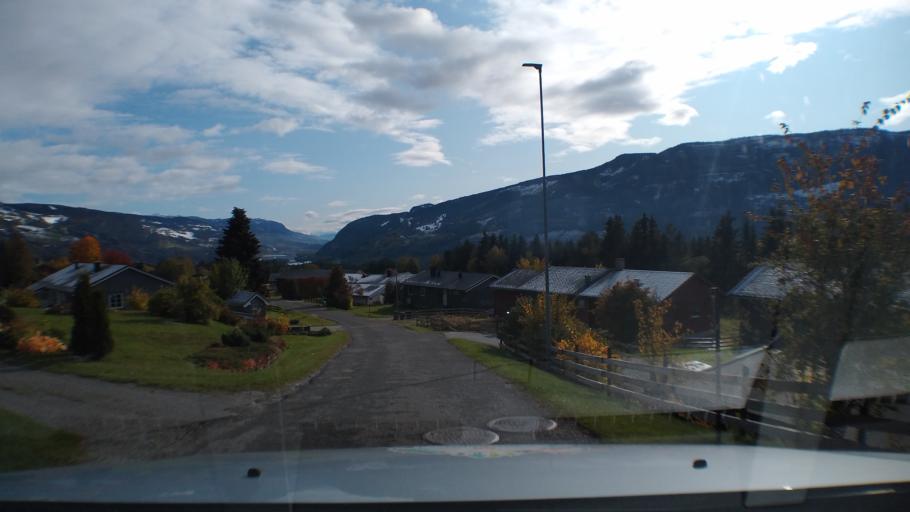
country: NO
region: Oppland
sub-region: Ringebu
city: Ringebu
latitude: 61.5420
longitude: 10.1193
